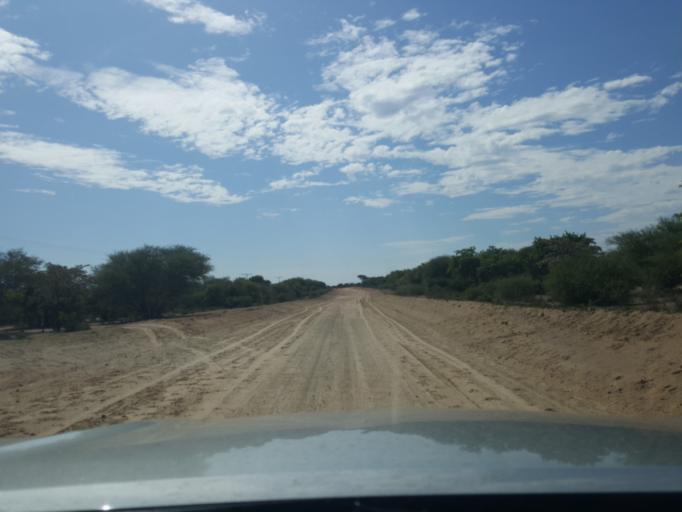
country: BW
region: Kweneng
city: Khudumelapye
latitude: -23.8649
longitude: 24.8898
